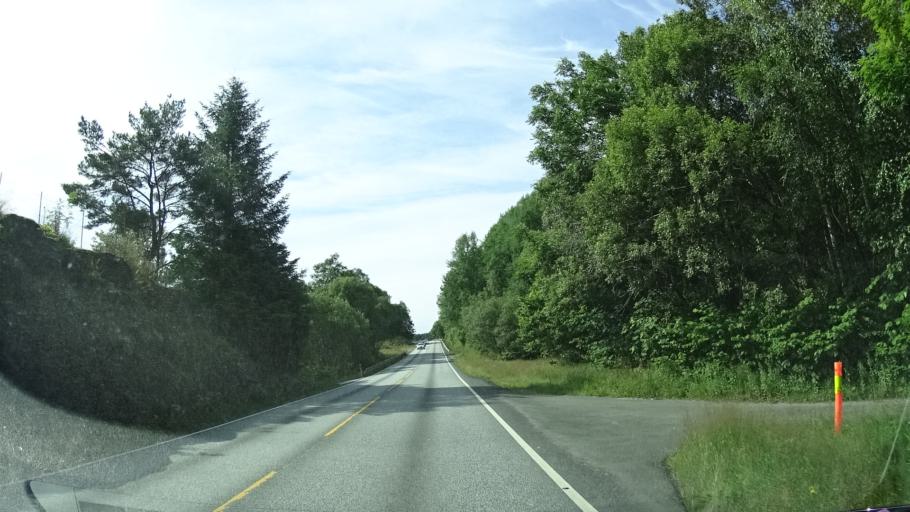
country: NO
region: Hordaland
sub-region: Sveio
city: Sveio
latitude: 59.5921
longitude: 5.4447
